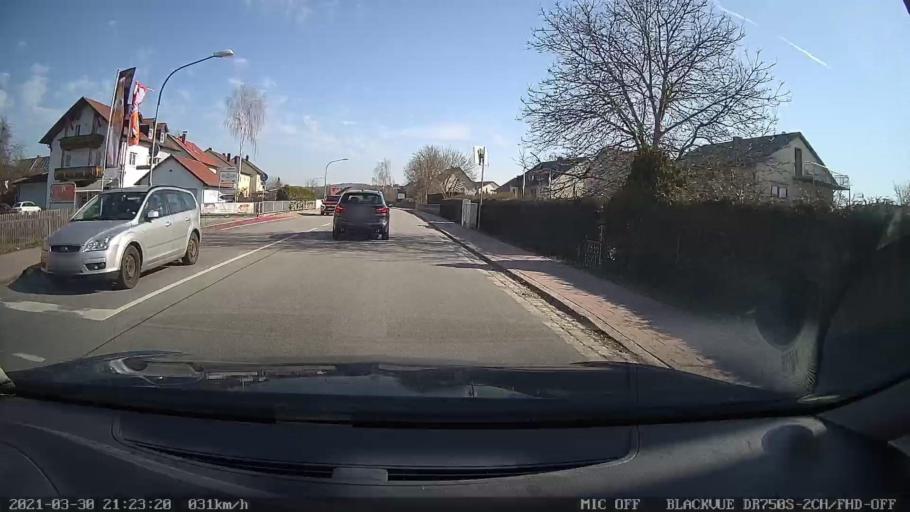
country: DE
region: Bavaria
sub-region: Upper Palatinate
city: Zeitlarn
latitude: 49.0798
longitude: 12.1129
